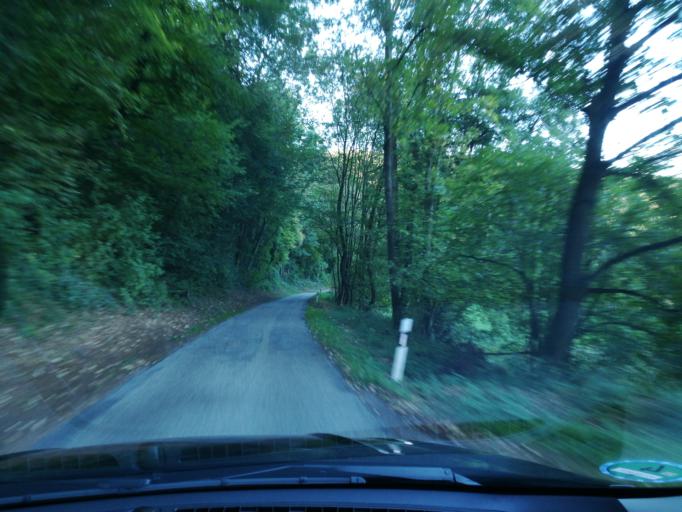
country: DE
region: Bavaria
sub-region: Lower Bavaria
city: Essing
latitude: 48.8975
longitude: 11.8159
